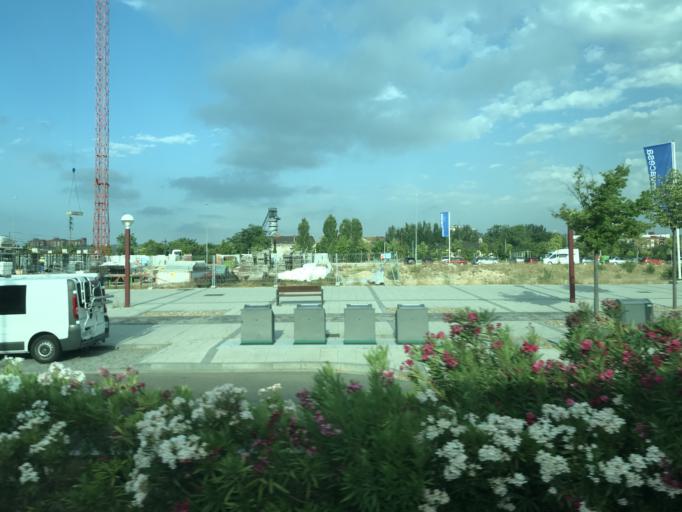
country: ES
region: Castille and Leon
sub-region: Provincia de Valladolid
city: Valladolid
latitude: 41.6354
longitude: -4.7295
